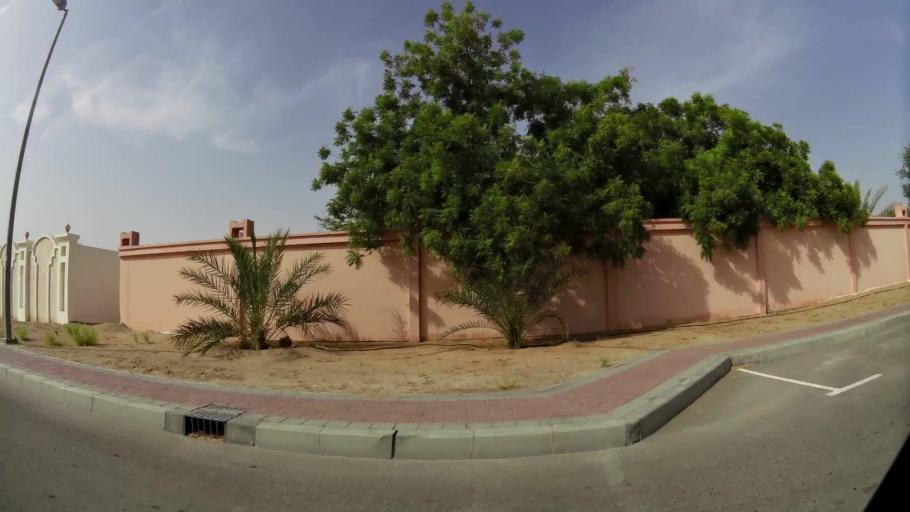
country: AE
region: Abu Dhabi
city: Al Ain
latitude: 24.1341
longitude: 55.7047
